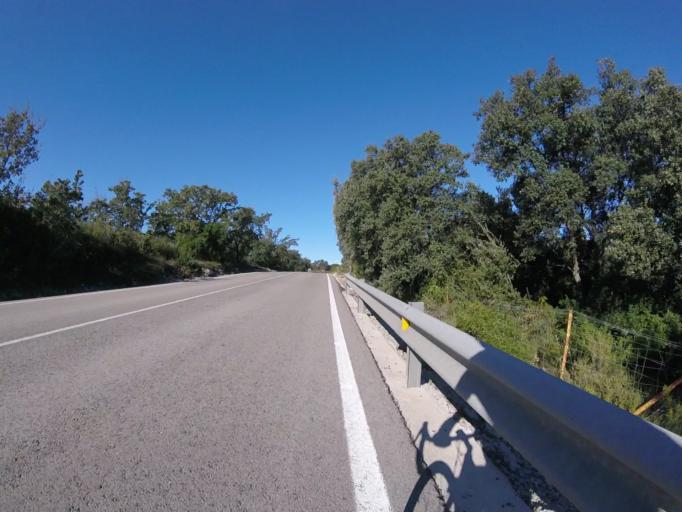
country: ES
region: Valencia
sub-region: Provincia de Castello
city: Cervera del Maestre
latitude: 40.4735
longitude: 0.2332
